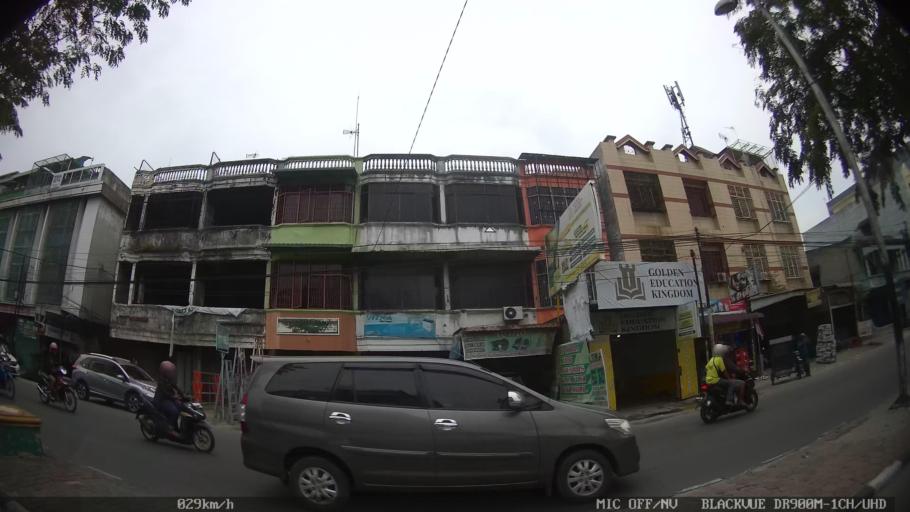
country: ID
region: North Sumatra
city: Deli Tua
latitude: 3.5425
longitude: 98.6860
